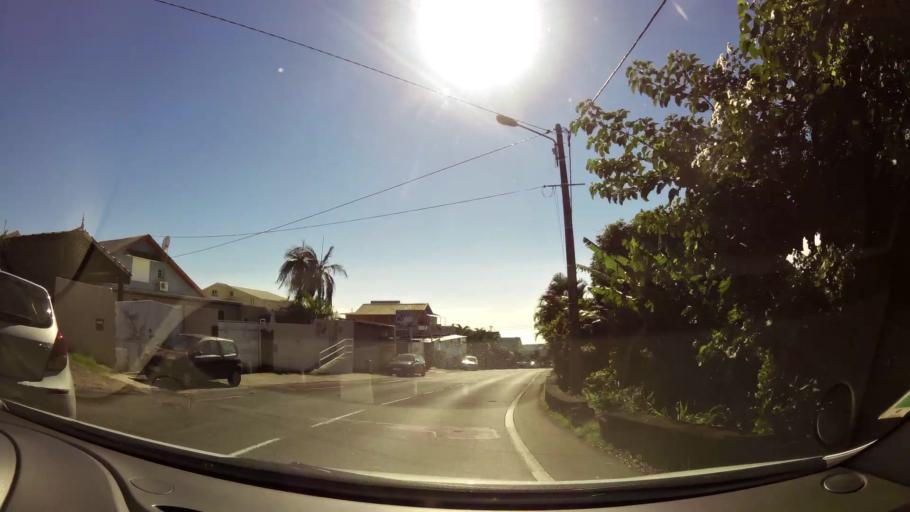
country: RE
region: Reunion
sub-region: Reunion
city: Saint-Denis
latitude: -20.9130
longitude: 55.4837
